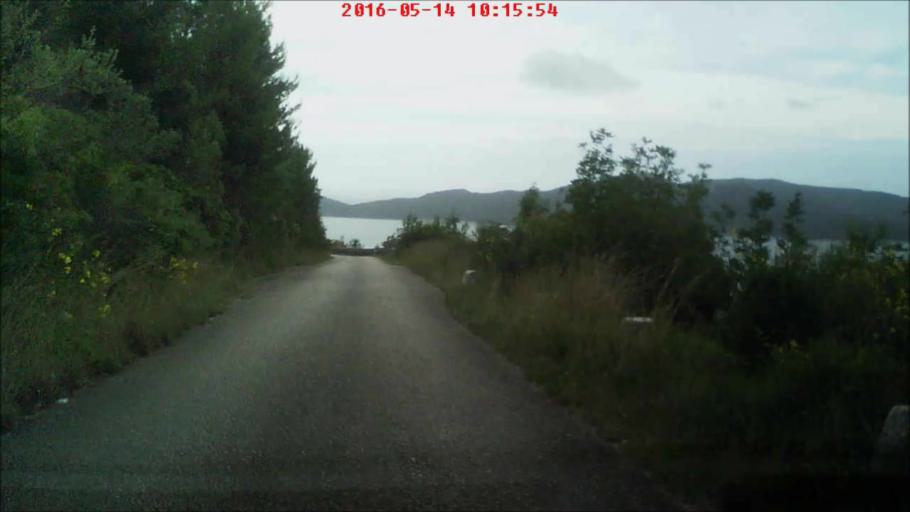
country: HR
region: Dubrovacko-Neretvanska
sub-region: Grad Dubrovnik
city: Mokosica
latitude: 42.7282
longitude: 17.9628
